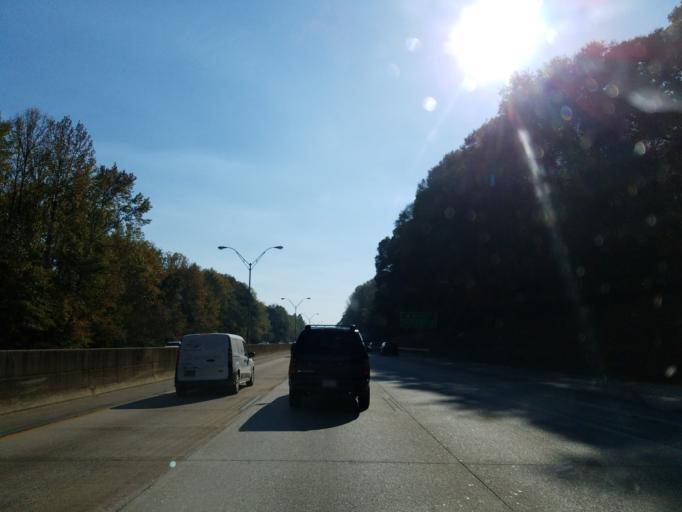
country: US
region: Georgia
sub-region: Fulton County
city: Hapeville
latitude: 33.6779
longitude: -84.4128
